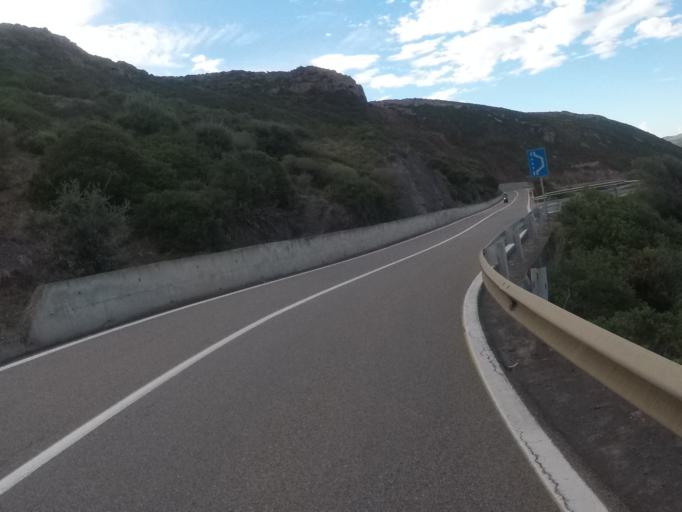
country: IT
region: Sardinia
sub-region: Provincia di Carbonia-Iglesias
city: Gonnesa
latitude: 39.3050
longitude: 8.4360
